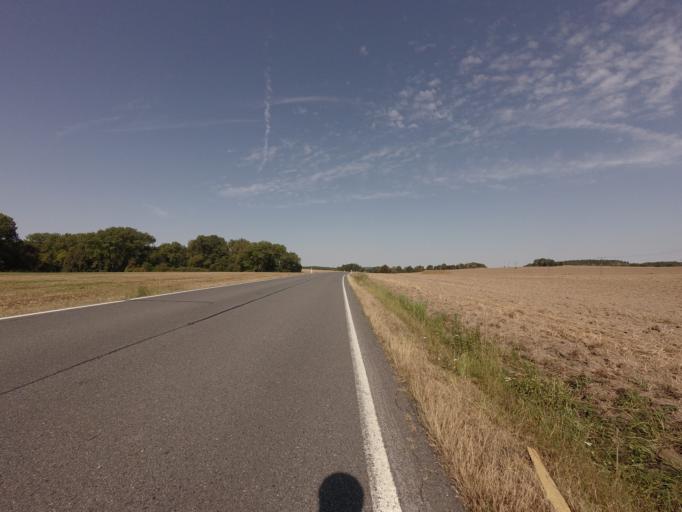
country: CZ
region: Jihocesky
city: Bernartice
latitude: 49.3760
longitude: 14.3730
